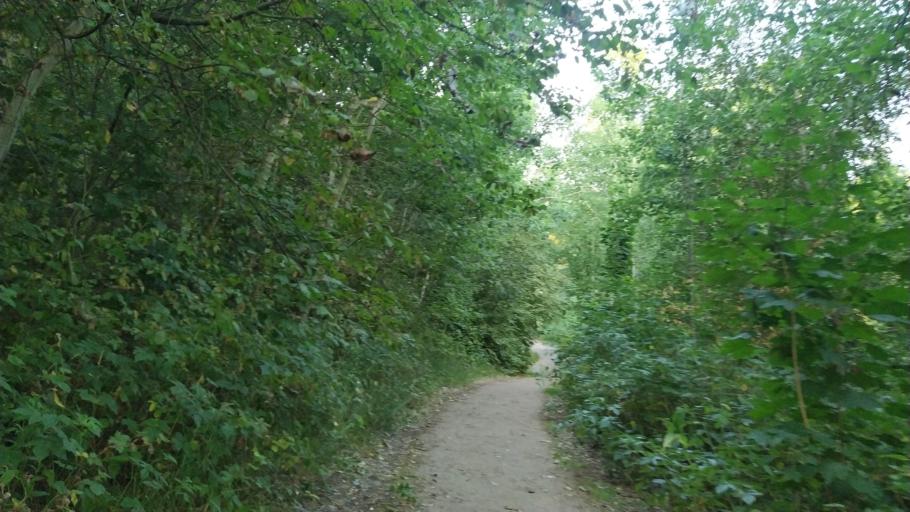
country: RU
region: St.-Petersburg
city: Kronshtadt
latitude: 60.0255
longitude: 29.6712
